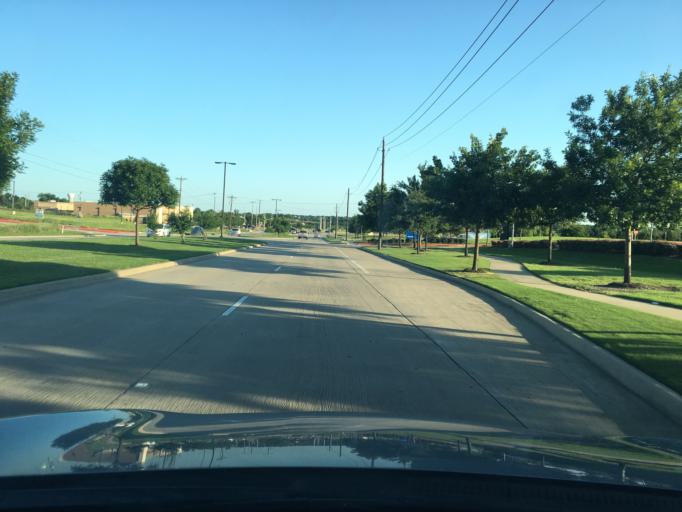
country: US
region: Texas
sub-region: Collin County
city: McKinney
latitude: 33.2212
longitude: -96.6793
